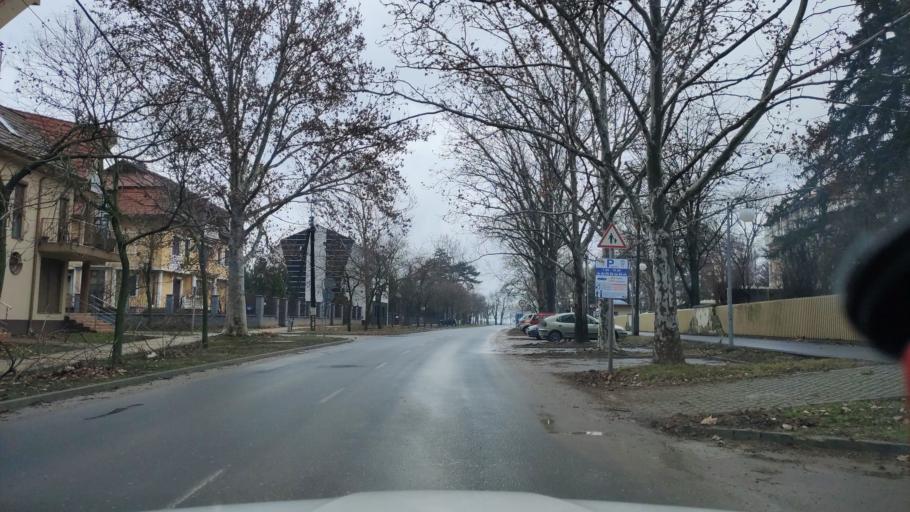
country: HU
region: Hajdu-Bihar
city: Hajduszoboszlo
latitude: 47.4531
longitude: 21.3939
